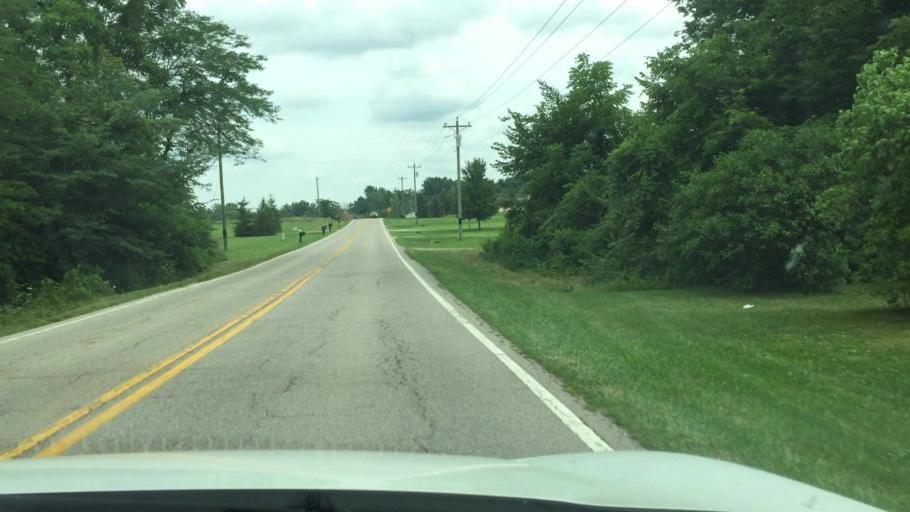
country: US
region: Ohio
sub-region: Union County
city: Marysville
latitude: 40.2274
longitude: -83.4597
